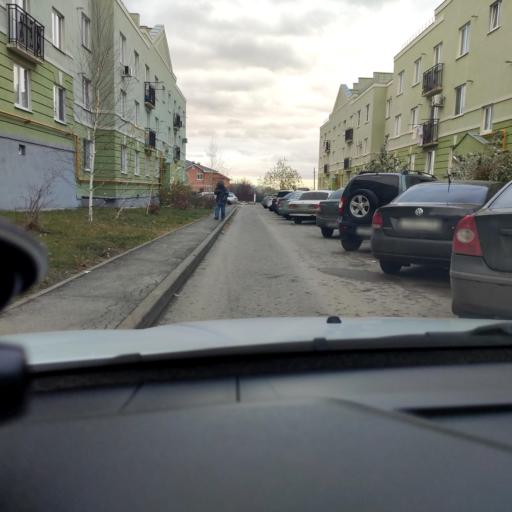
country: RU
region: Samara
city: Petra-Dubrava
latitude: 53.3115
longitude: 50.3113
